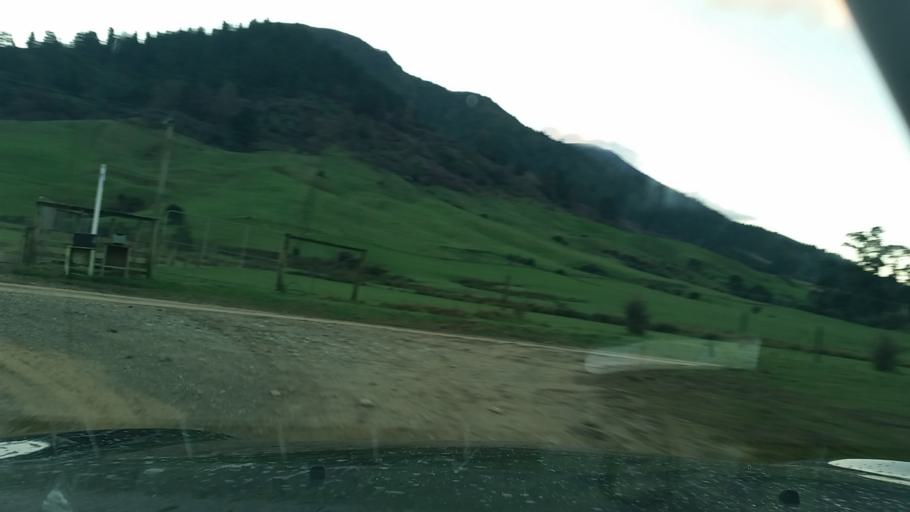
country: NZ
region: Marlborough
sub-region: Marlborough District
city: Picton
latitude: -41.1557
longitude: 174.1298
